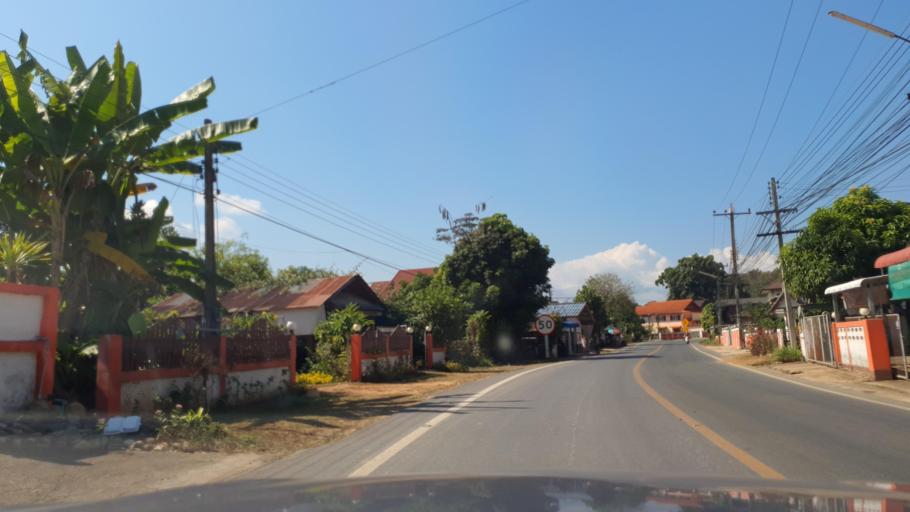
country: TH
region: Nan
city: Tha Wang Pha
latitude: 19.0817
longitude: 100.8821
